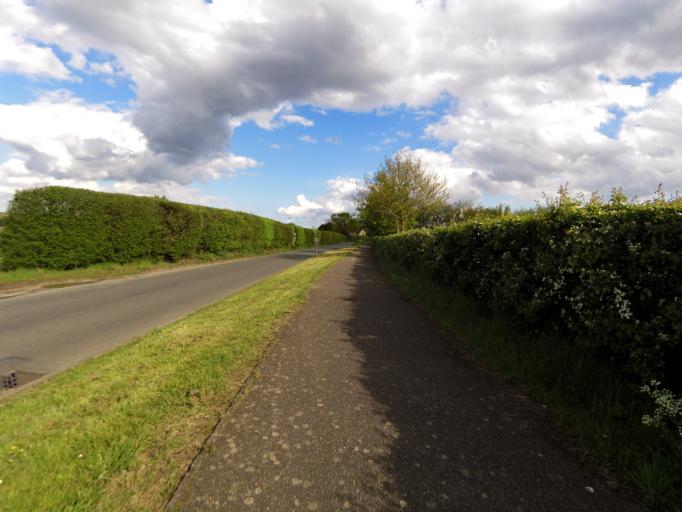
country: GB
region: England
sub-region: Suffolk
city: Woolpit
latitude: 52.2202
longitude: 0.8977
